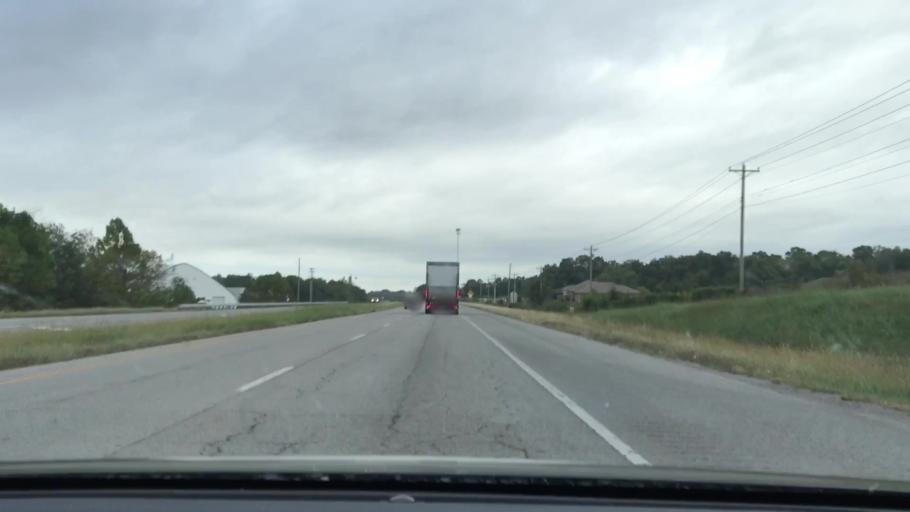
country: US
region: Kentucky
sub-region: Christian County
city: Hopkinsville
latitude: 36.8280
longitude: -87.5148
